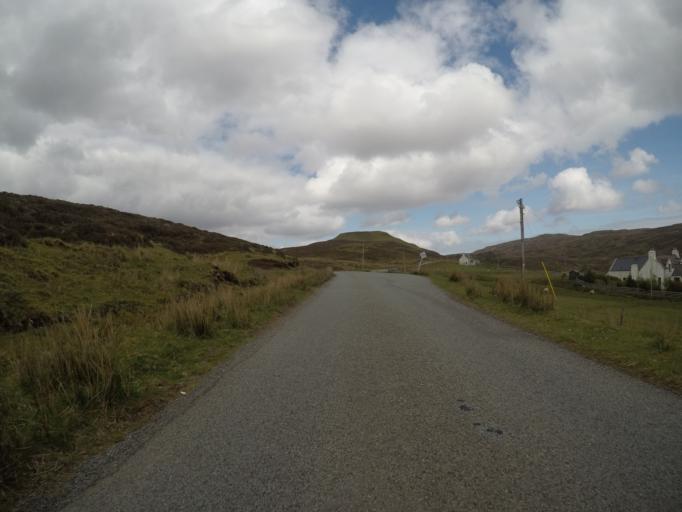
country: GB
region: Scotland
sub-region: Highland
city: Isle of Skye
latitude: 57.3738
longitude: -6.3765
